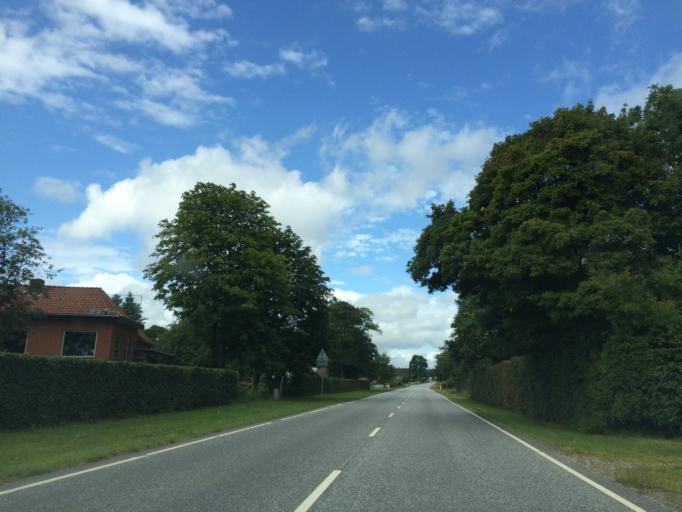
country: DK
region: Central Jutland
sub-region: Silkeborg Kommune
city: Svejbaek
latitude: 56.1881
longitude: 9.7001
